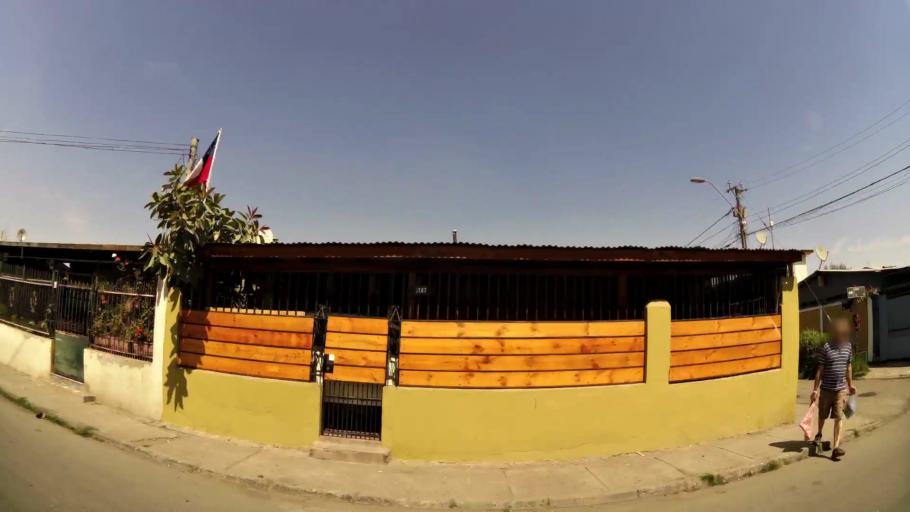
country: CL
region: Santiago Metropolitan
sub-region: Provincia de Santiago
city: La Pintana
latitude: -33.5442
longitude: -70.6454
